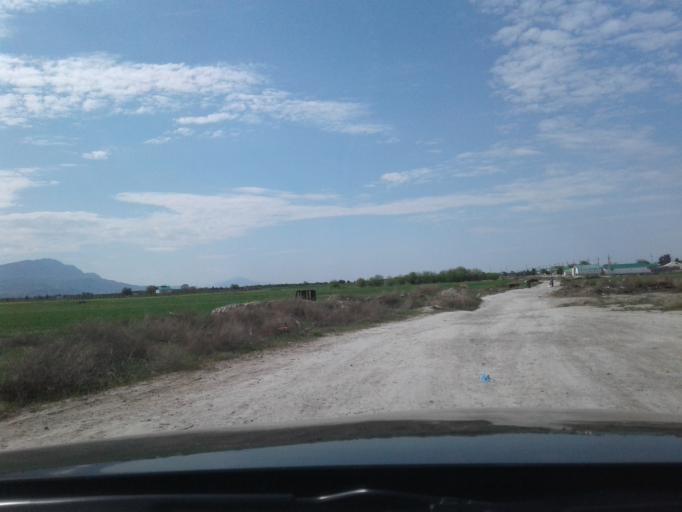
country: TM
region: Ahal
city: Ashgabat
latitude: 37.9786
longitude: 58.2915
